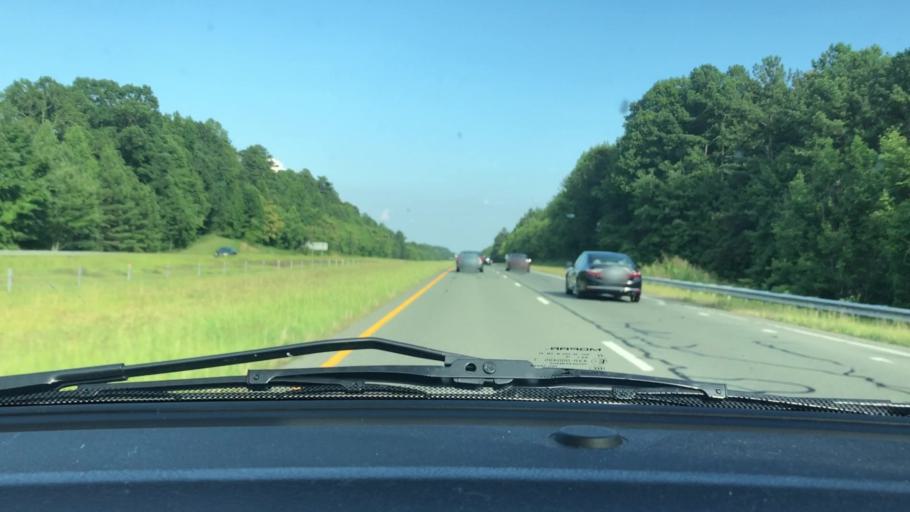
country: US
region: North Carolina
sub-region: Chatham County
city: Siler City
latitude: 35.7598
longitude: -79.4668
